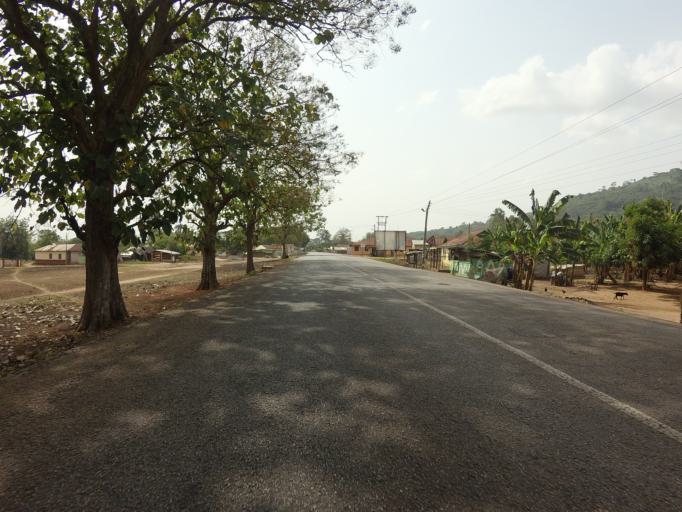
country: GH
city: Akropong
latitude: 6.2819
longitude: 0.1320
